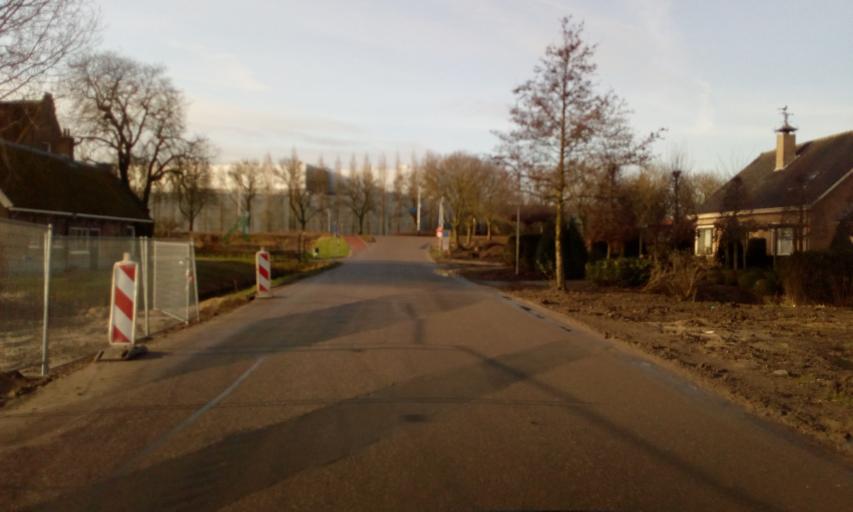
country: NL
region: South Holland
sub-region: Gemeente Zwijndrecht
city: Heerjansdam
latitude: 51.8626
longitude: 4.5644
